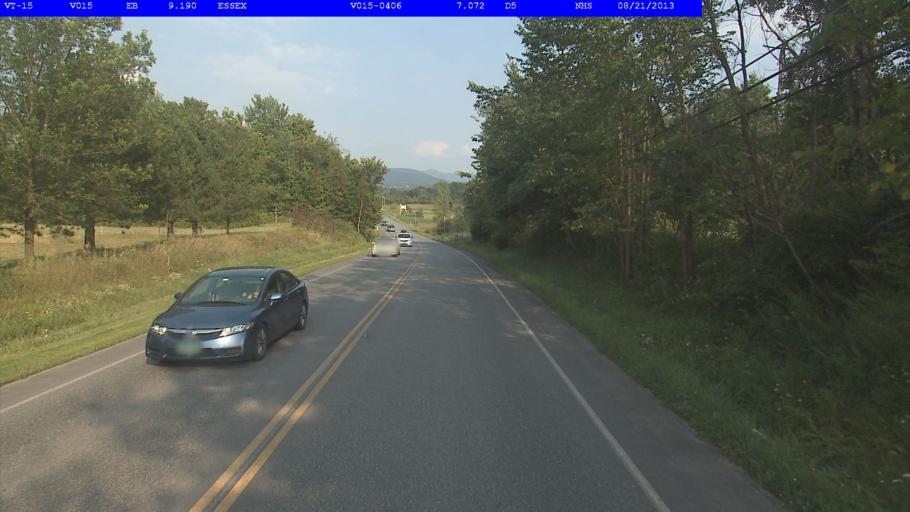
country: US
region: Vermont
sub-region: Chittenden County
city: Jericho
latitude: 44.5019
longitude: -73.0282
